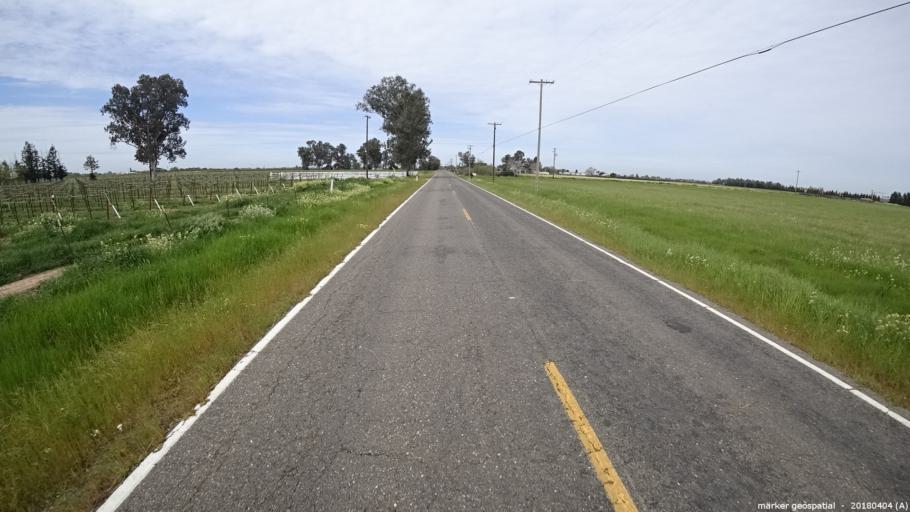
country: US
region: California
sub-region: Sacramento County
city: Herald
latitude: 38.2633
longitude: -121.2116
